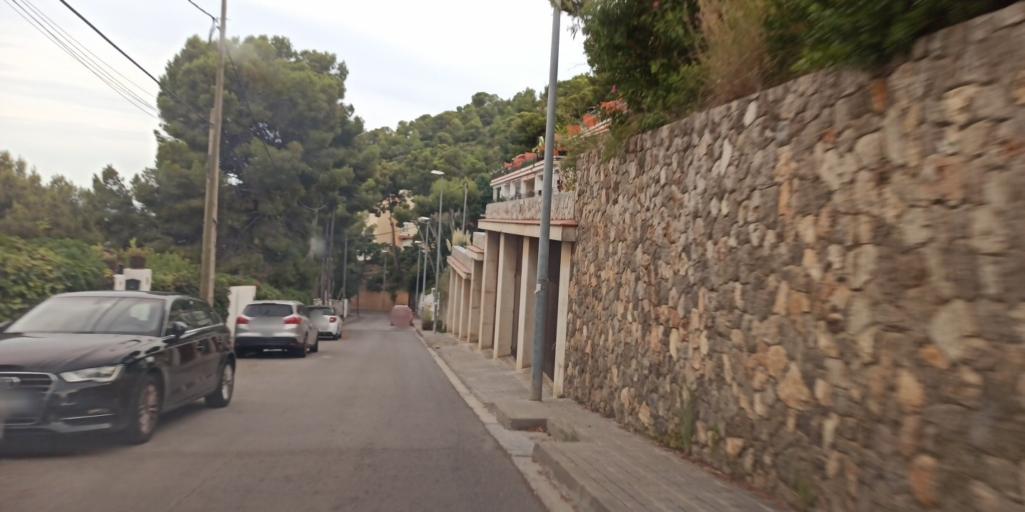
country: ES
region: Catalonia
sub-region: Provincia de Barcelona
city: Castelldefels
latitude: 41.2702
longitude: 1.9414
